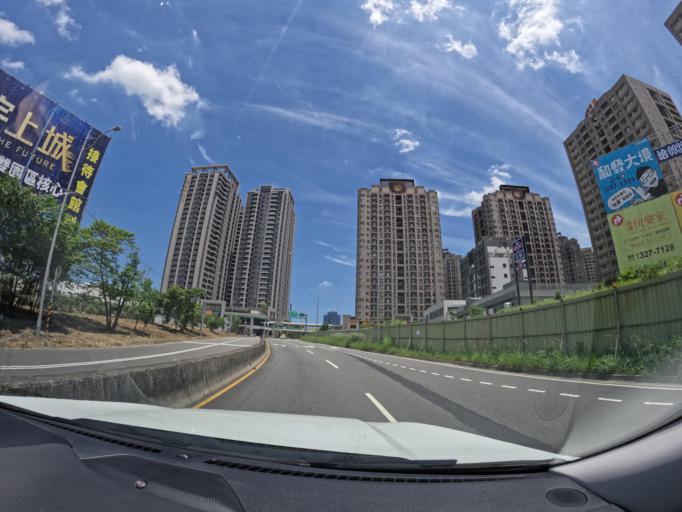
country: TW
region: Taipei
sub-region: Taipei
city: Banqiao
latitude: 25.0391
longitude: 121.3872
